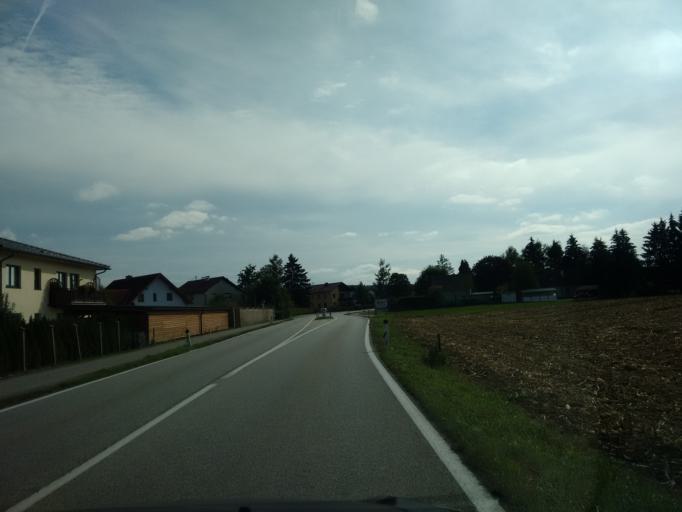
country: AT
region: Upper Austria
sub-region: Politischer Bezirk Steyr-Land
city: Bad Hall
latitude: 48.0759
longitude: 14.1913
